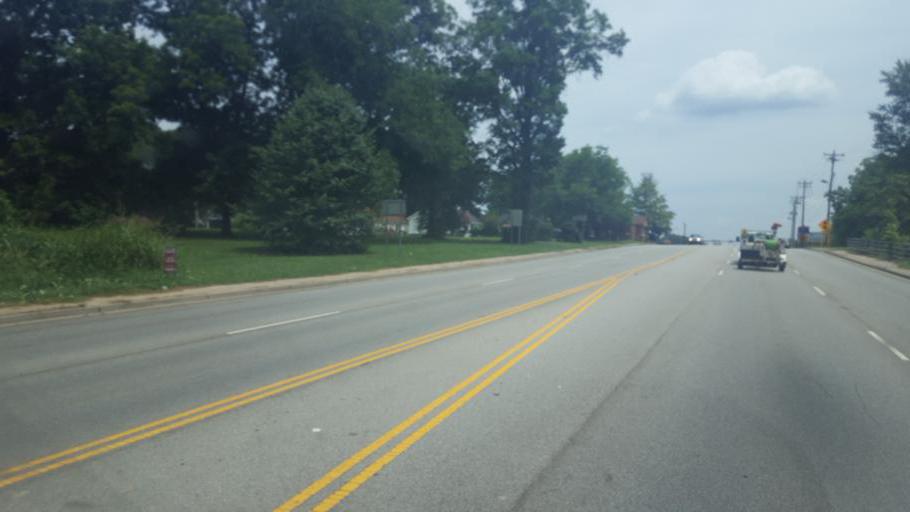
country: US
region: South Carolina
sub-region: York County
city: Rock Hill
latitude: 34.9378
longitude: -81.0453
